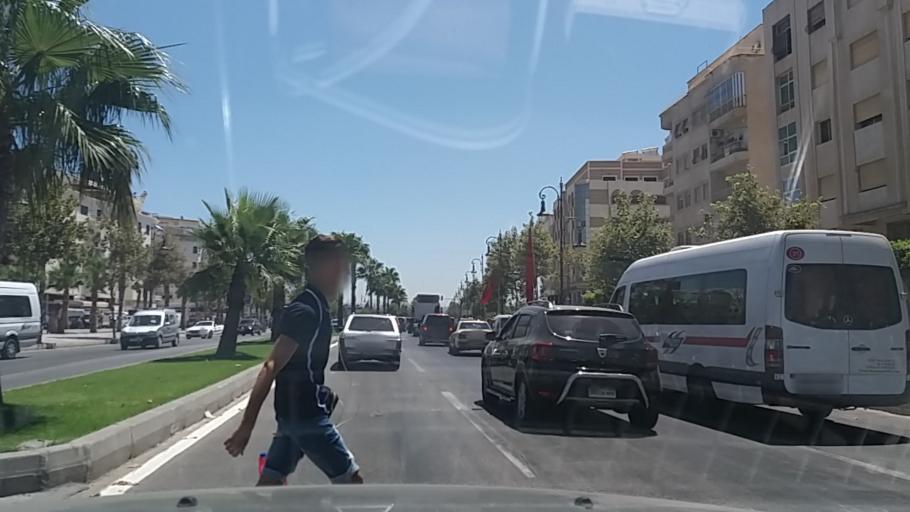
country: MA
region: Tanger-Tetouan
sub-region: Tanger-Assilah
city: Tangier
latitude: 35.7585
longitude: -5.7929
